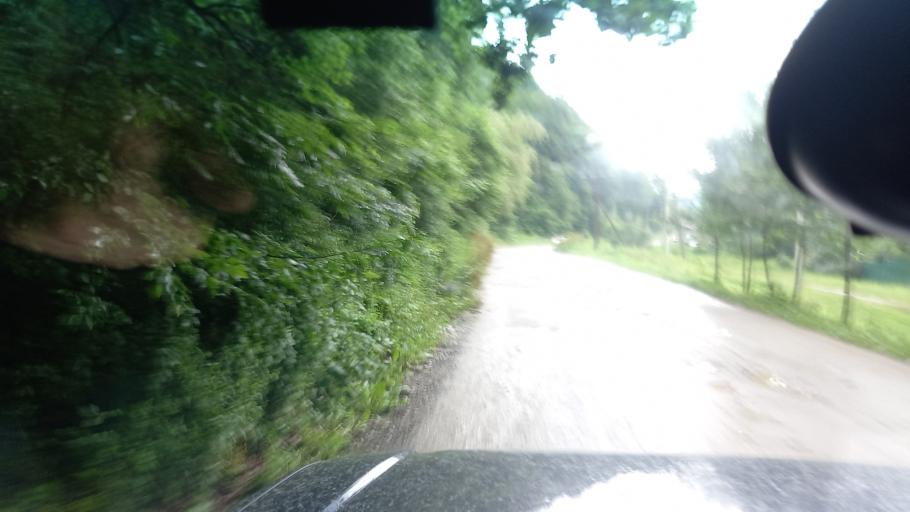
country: RU
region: Krasnodarskiy
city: Psebay
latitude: 44.0428
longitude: 40.7575
